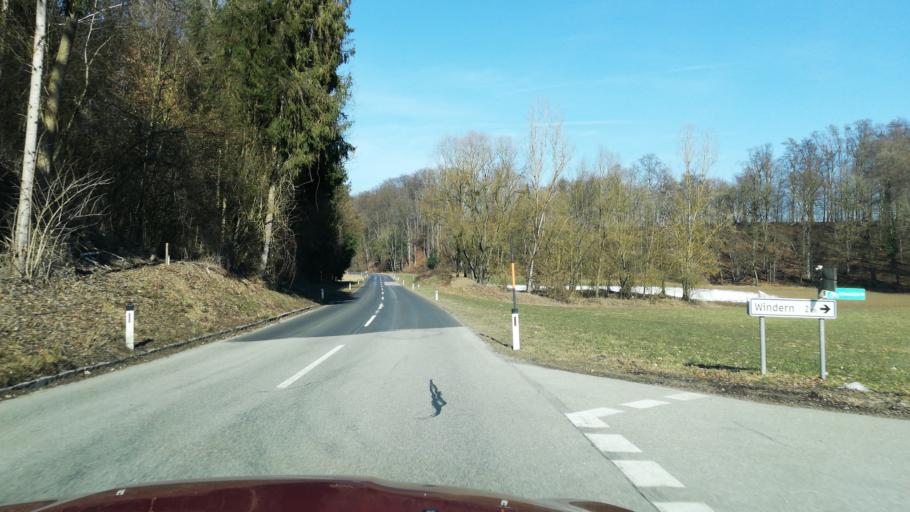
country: AT
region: Upper Austria
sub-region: Politischer Bezirk Vocklabruck
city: Desselbrunn
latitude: 48.0247
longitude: 13.7743
